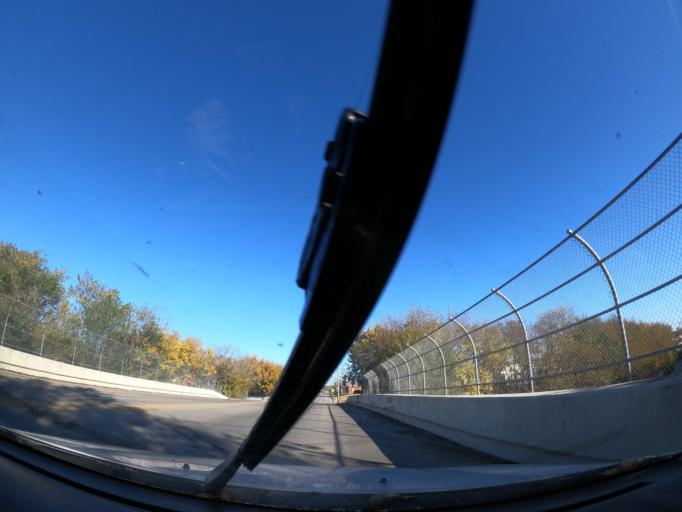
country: US
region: Oklahoma
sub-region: Tulsa County
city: Tulsa
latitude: 36.1651
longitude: -95.9671
